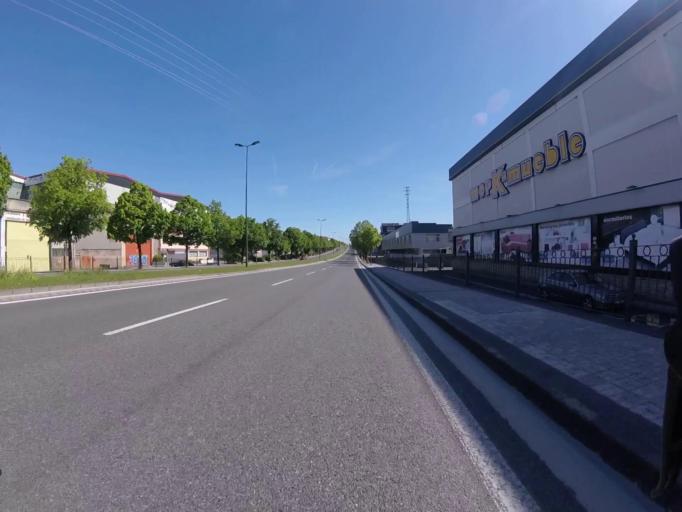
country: ES
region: Basque Country
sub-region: Provincia de Guipuzcoa
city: Irun
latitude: 43.3352
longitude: -1.8150
